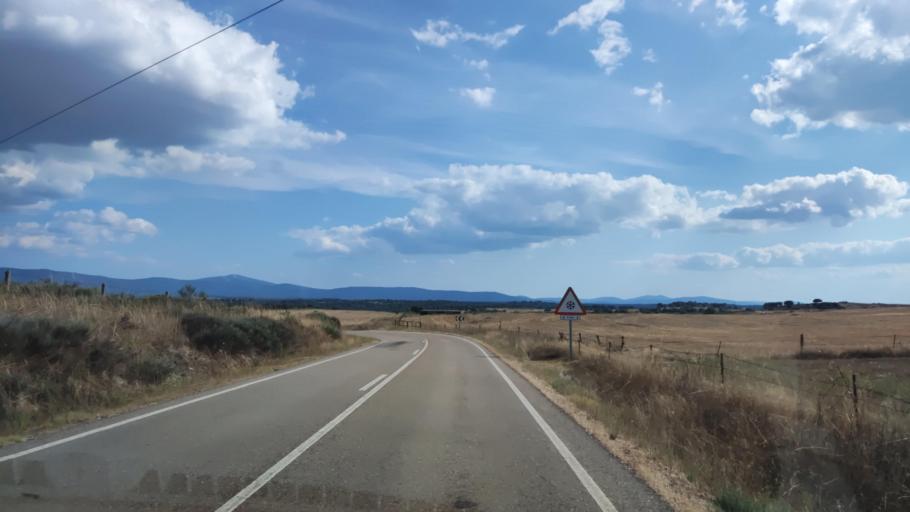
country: ES
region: Castille and Leon
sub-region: Provincia de Salamanca
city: Pastores
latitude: 40.5066
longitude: -6.5042
